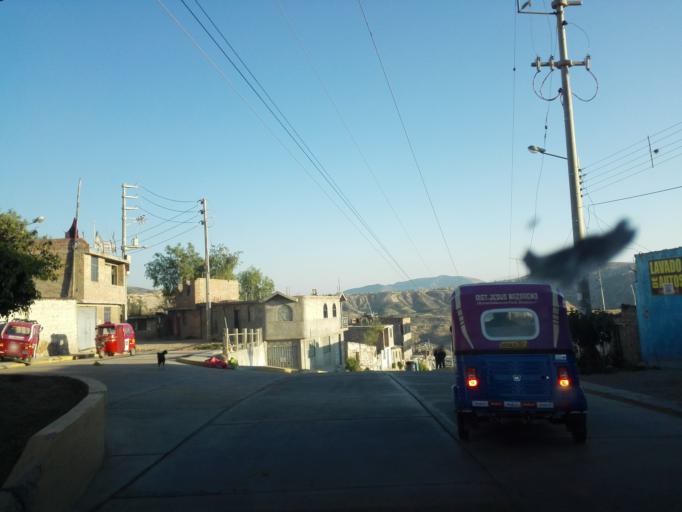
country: PE
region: Ayacucho
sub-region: Provincia de Huamanga
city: Ayacucho
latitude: -13.1467
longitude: -74.2153
